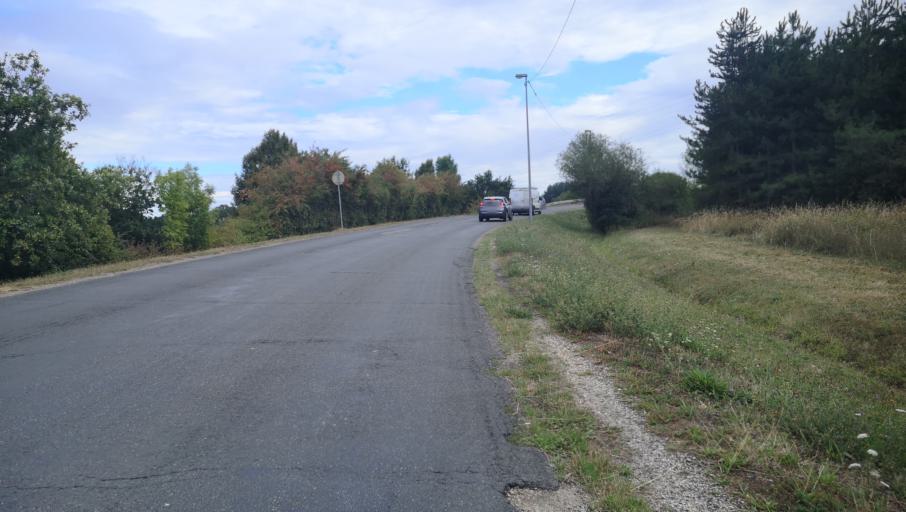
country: FR
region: Centre
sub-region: Departement du Loiret
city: Boigny-sur-Bionne
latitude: 47.9215
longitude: 2.0004
